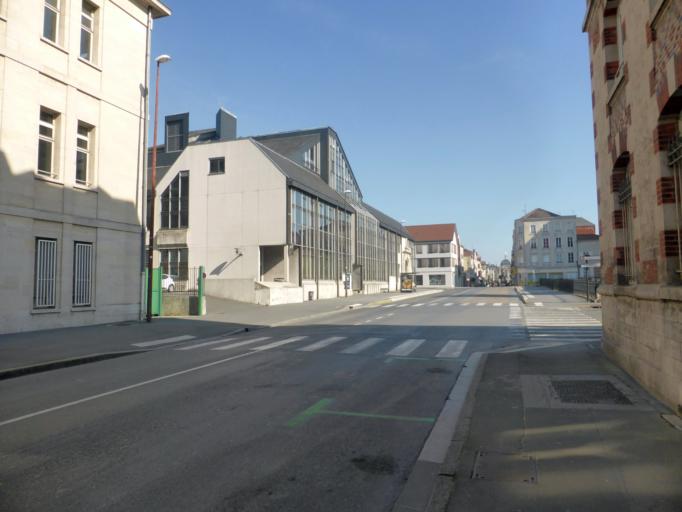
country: FR
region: Champagne-Ardenne
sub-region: Departement de la Marne
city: Chalons-en-Champagne
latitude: 48.9554
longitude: 4.3559
